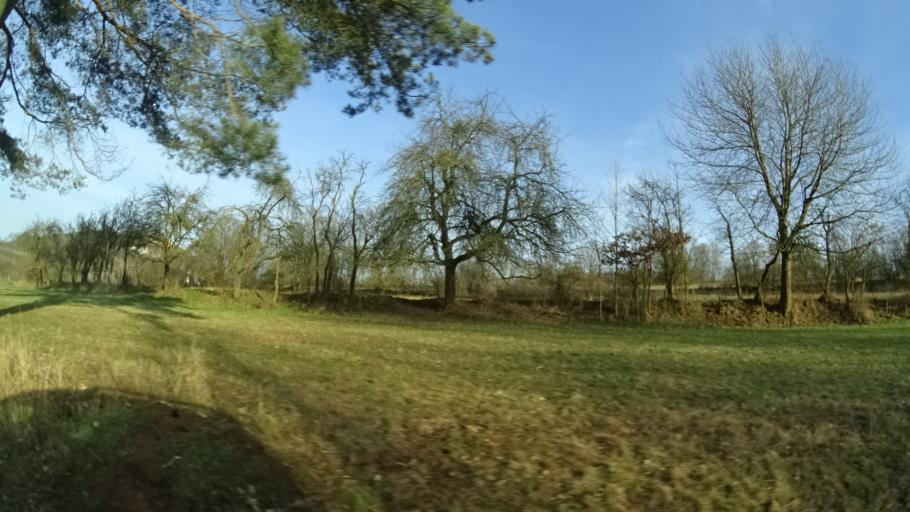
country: DE
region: Bavaria
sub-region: Regierungsbezirk Unterfranken
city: Zeitlofs
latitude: 50.2964
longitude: 9.6608
